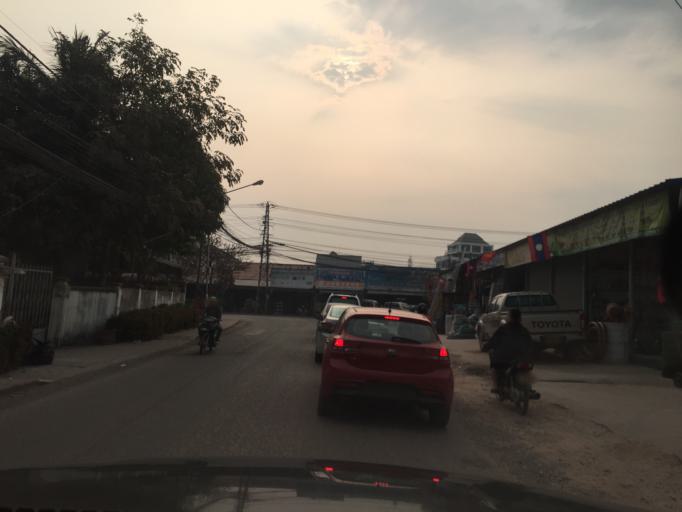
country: LA
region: Vientiane
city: Vientiane
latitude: 17.9737
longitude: 102.6017
